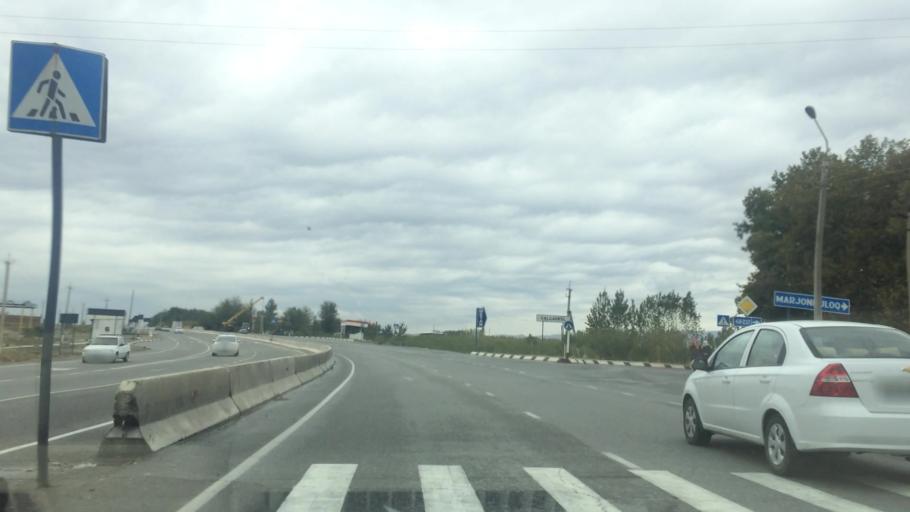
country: UZ
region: Jizzax
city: Jizzax
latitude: 39.9775
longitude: 67.5631
